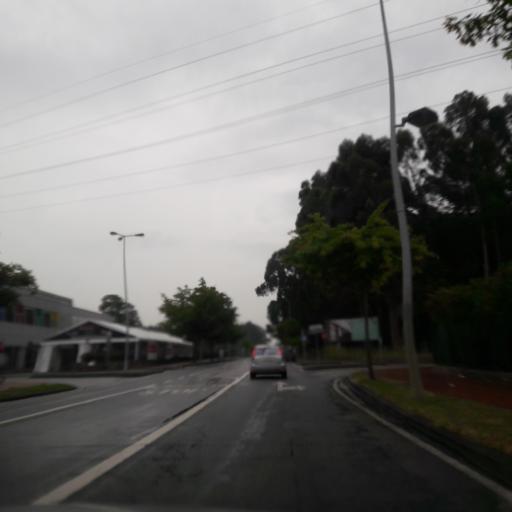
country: PT
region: Porto
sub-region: Vila do Conde
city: Arvore
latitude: 41.3235
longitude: -8.7147
